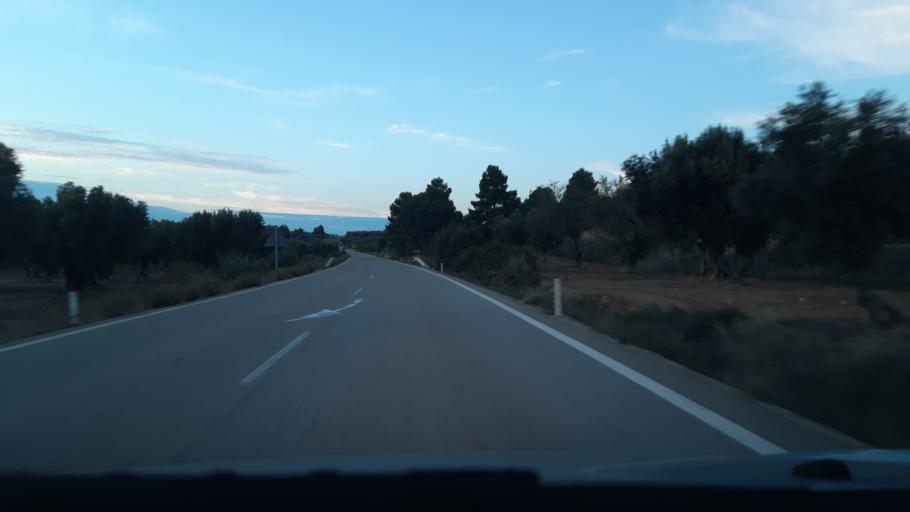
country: ES
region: Aragon
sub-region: Provincia de Teruel
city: Valderrobres
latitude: 40.8550
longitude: 0.1725
